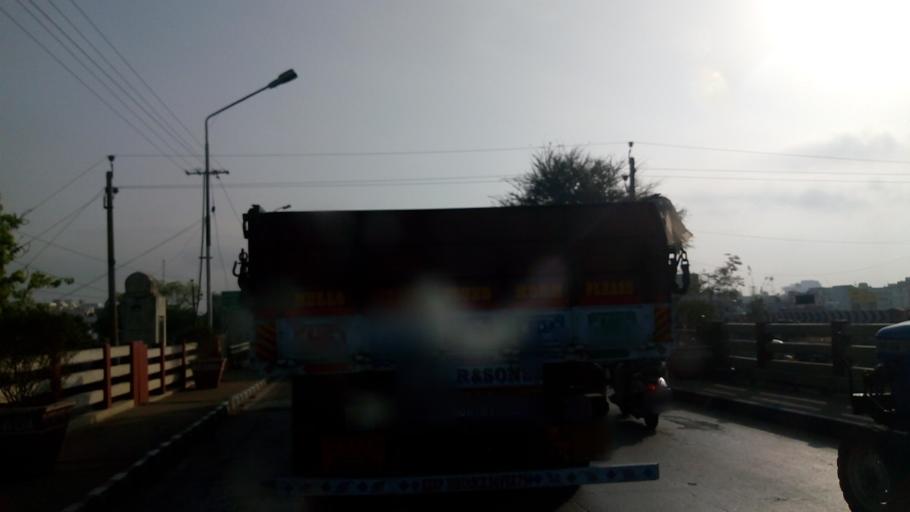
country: IN
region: Andhra Pradesh
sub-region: Krishna
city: Vijayawada
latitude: 16.4989
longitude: 80.6308
